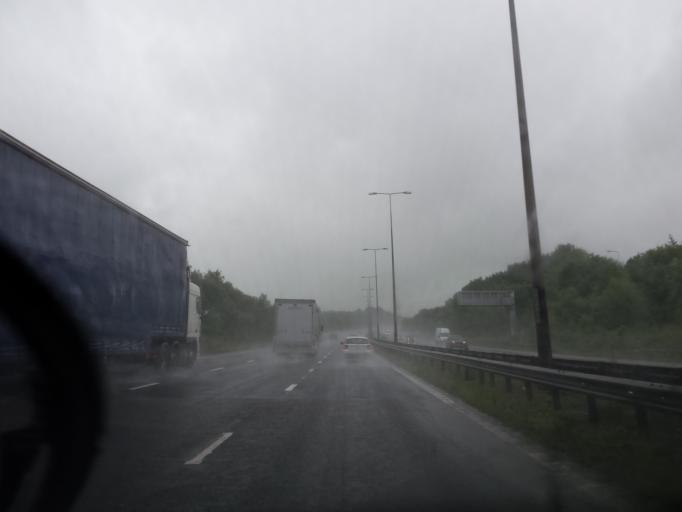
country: GB
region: England
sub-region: Leicestershire
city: Shepshed
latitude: 52.7597
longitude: -1.2739
